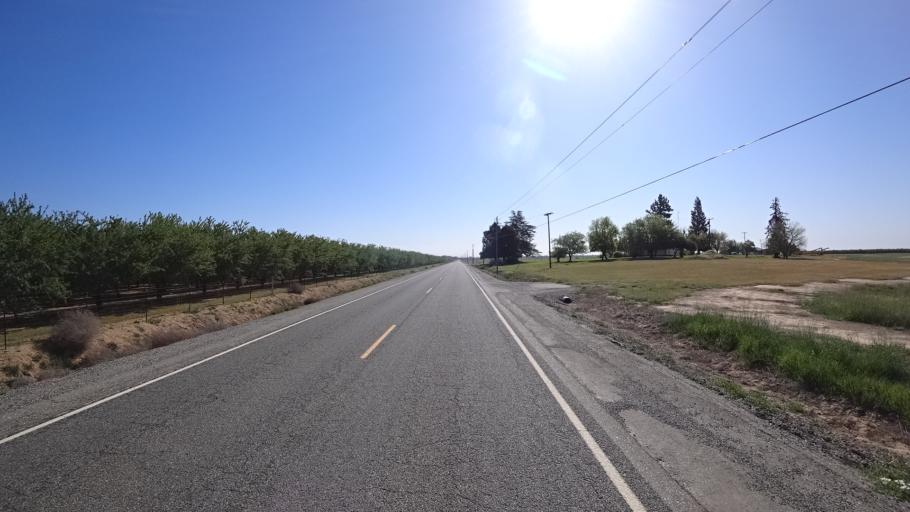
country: US
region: California
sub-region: Glenn County
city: Hamilton City
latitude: 39.7091
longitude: -122.0318
